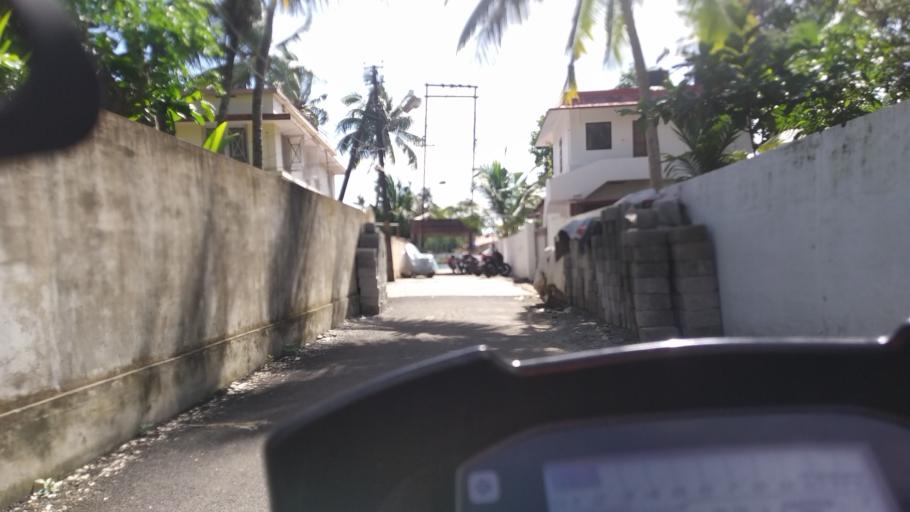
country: IN
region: Kerala
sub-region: Ernakulam
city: Elur
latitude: 10.0295
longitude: 76.2671
